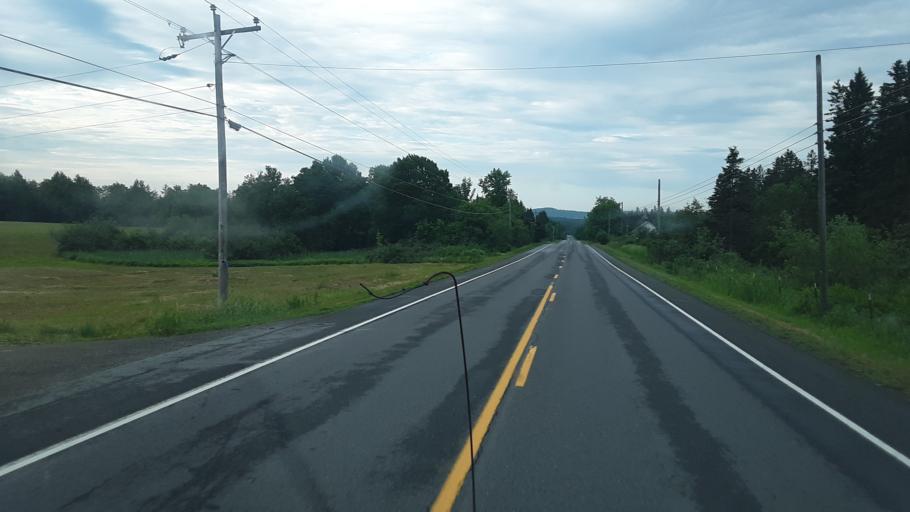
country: US
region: Maine
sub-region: Penobscot County
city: Patten
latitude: 45.9432
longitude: -68.4524
